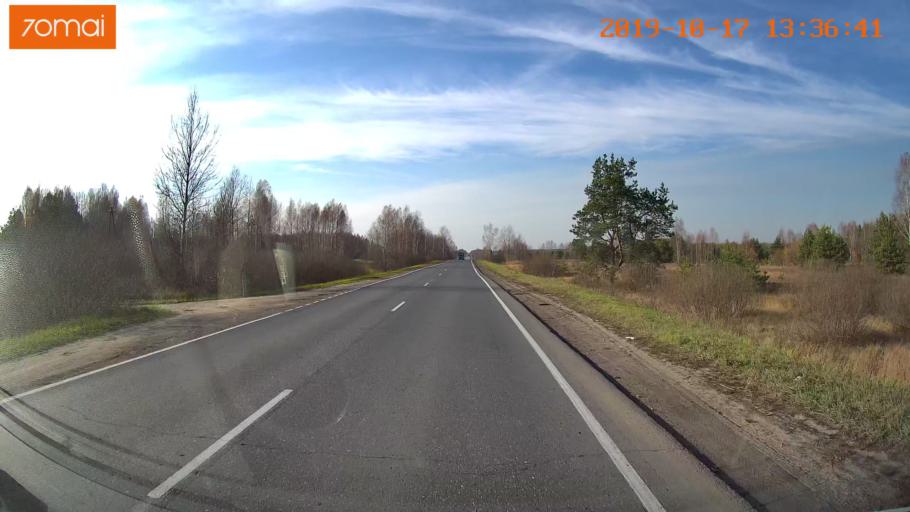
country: RU
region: Rjazan
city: Tuma
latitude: 55.1399
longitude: 40.6576
